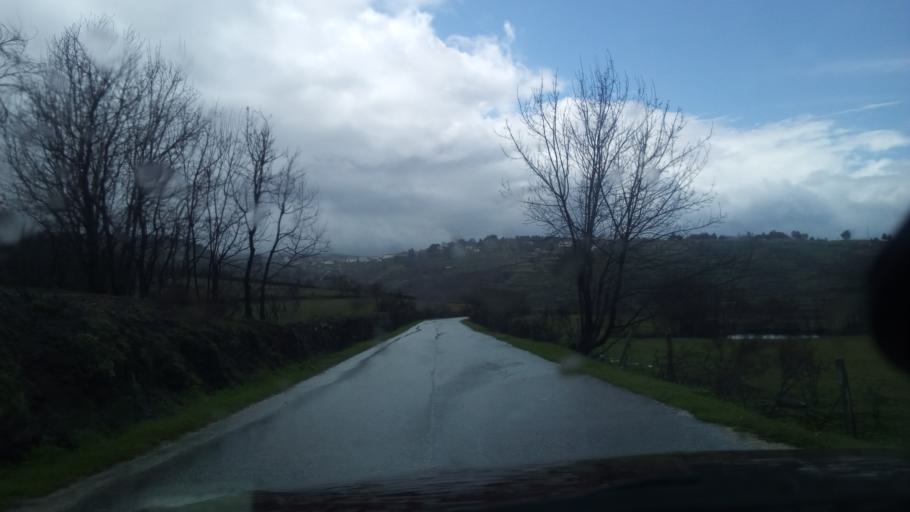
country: PT
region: Guarda
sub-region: Fornos de Algodres
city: Fornos de Algodres
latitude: 40.5513
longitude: -7.4750
